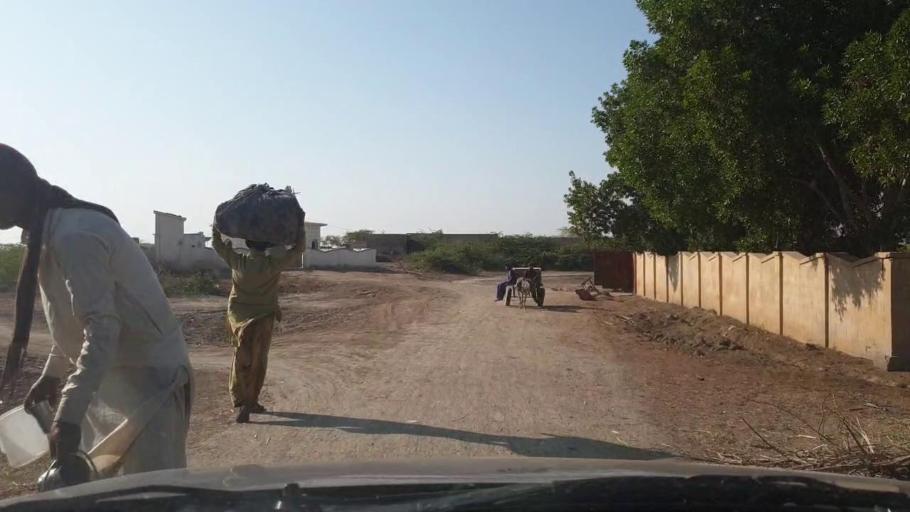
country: PK
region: Sindh
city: Digri
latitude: 25.1469
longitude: 69.2819
